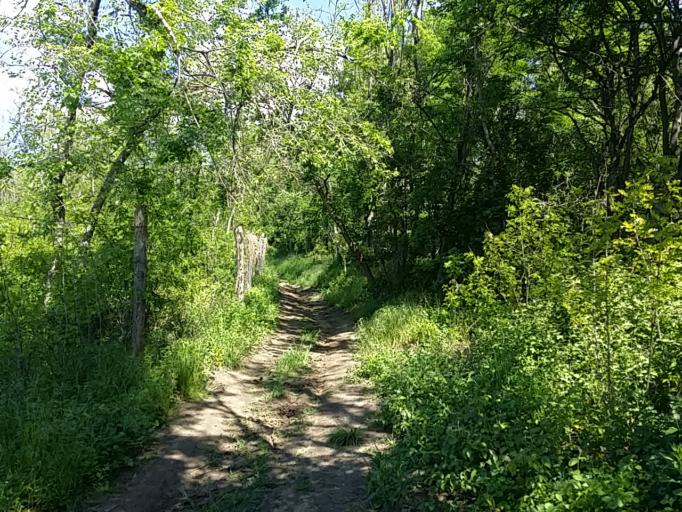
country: HU
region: Pest
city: Szada
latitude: 47.6400
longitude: 19.3344
